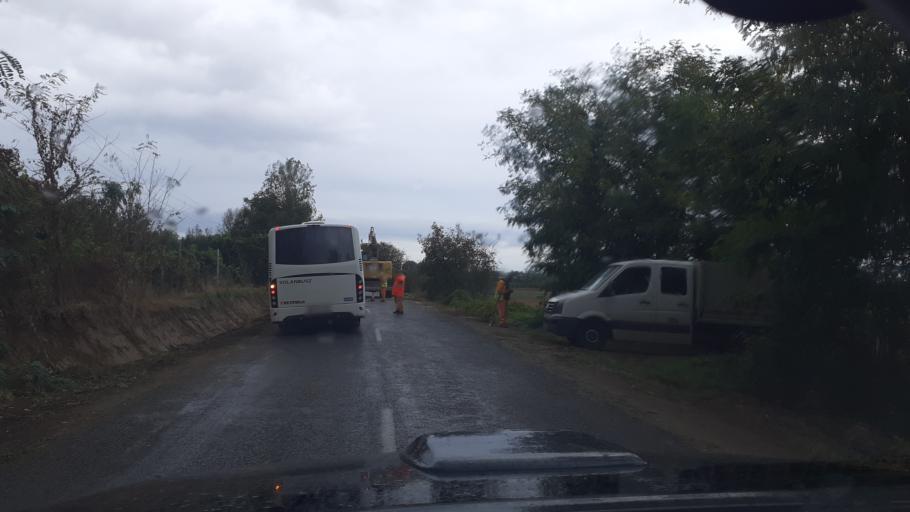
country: HU
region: Tolna
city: Bolcske
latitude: 46.7670
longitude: 18.9557
